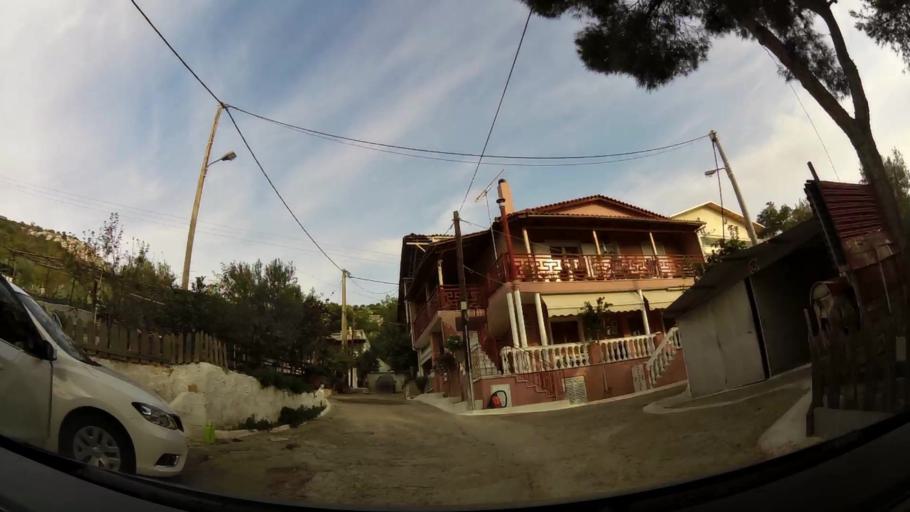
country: GR
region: Attica
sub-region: Nomarchia Athinas
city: Kamateron
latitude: 38.0608
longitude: 23.7008
